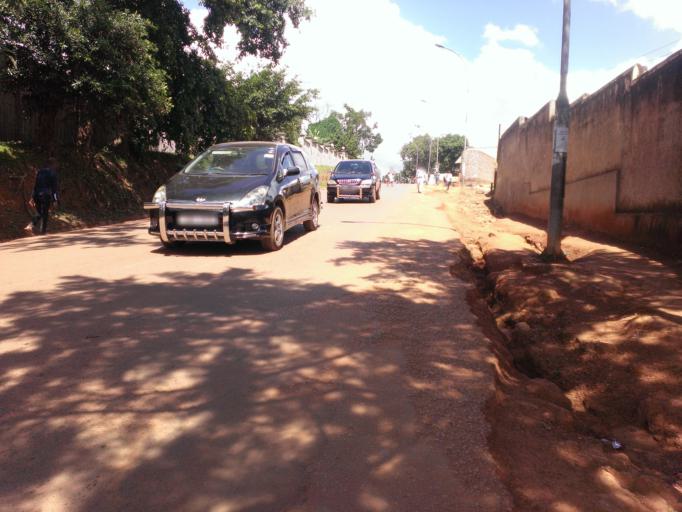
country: UG
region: Central Region
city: Kampala Central Division
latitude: 0.3307
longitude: 32.5543
